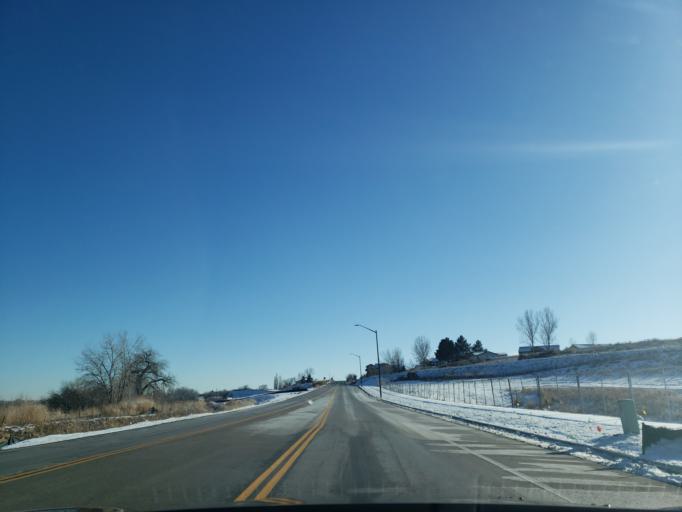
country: US
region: Colorado
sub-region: Larimer County
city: Fort Collins
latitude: 40.5180
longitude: -105.0012
